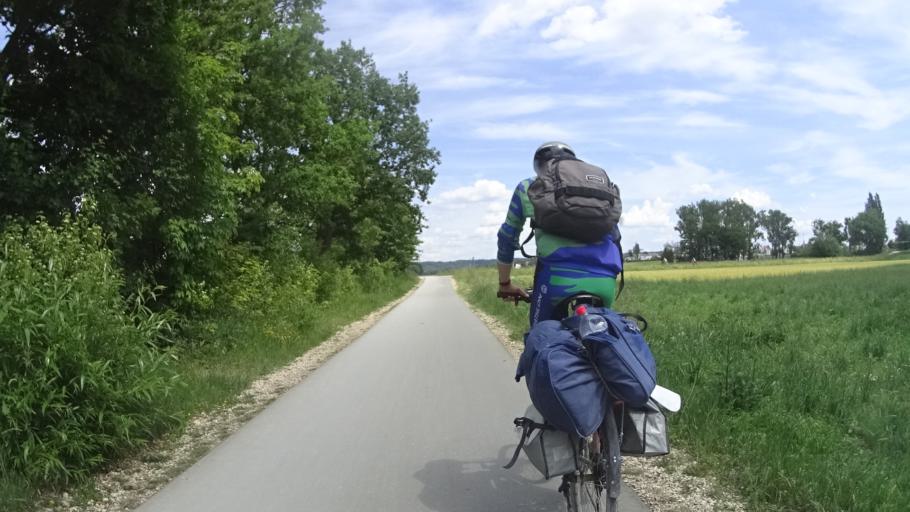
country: DE
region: Bavaria
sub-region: Upper Palatinate
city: Sinzing
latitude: 49.0136
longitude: 12.0306
